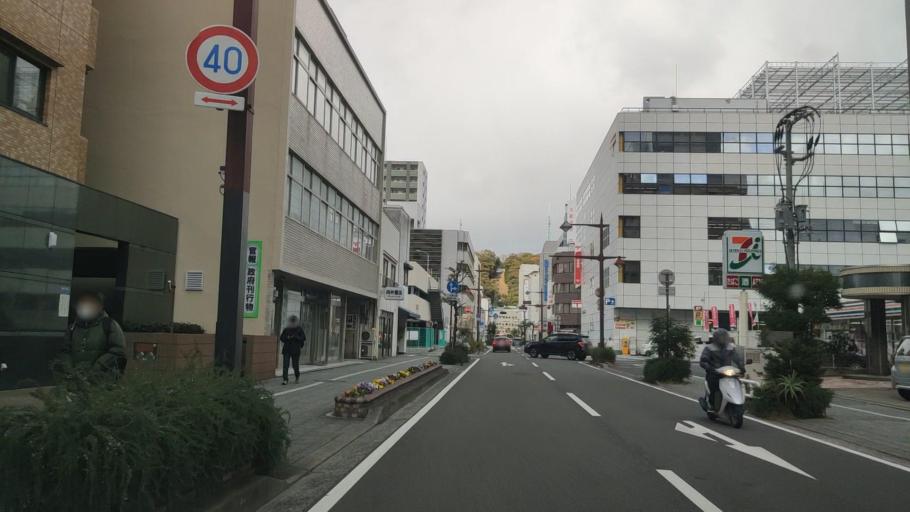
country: JP
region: Ehime
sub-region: Shikoku-chuo Shi
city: Matsuyama
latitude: 33.8373
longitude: 132.7679
